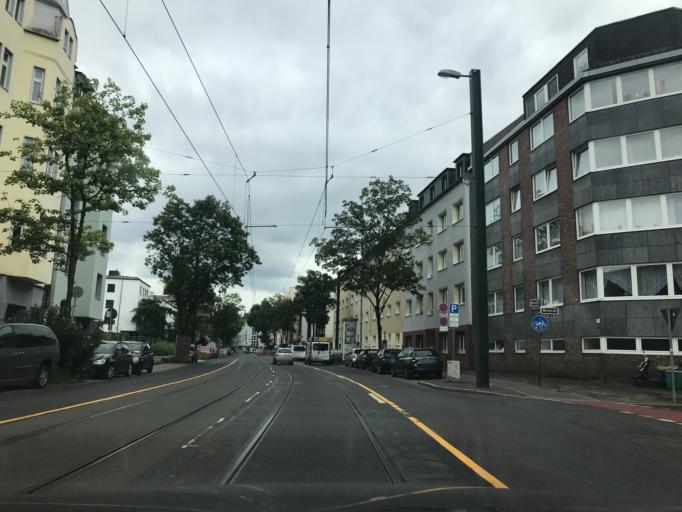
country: DE
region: North Rhine-Westphalia
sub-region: Regierungsbezirk Dusseldorf
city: Dusseldorf
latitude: 51.2498
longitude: 6.7821
